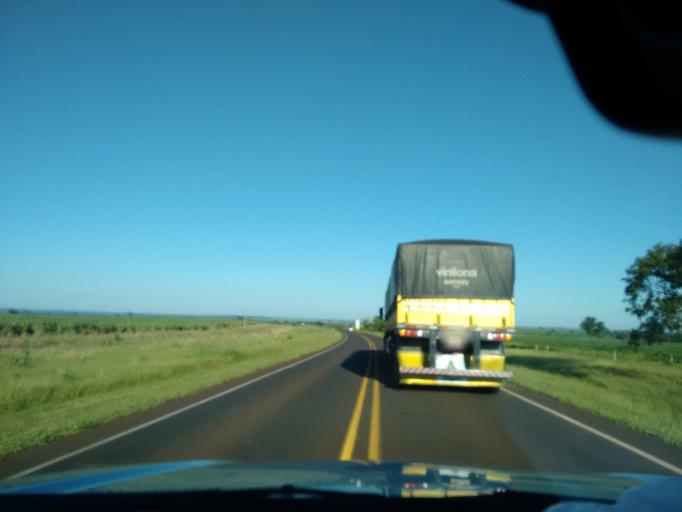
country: BR
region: Mato Grosso do Sul
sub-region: Caarapo
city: Caarapo
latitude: -22.8193
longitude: -54.6989
